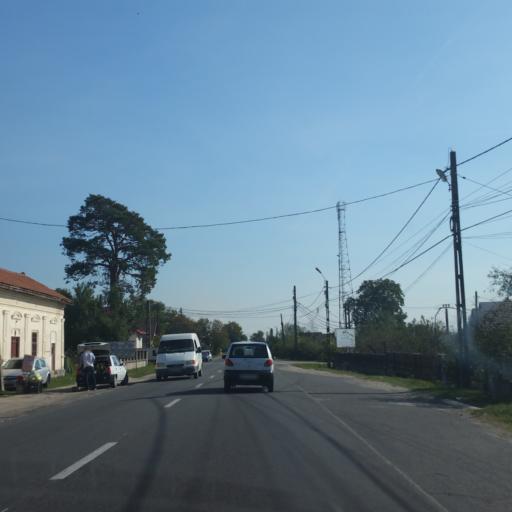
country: RO
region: Arges
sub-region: Comuna Baiculesti
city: Baiculesti
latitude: 45.0915
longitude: 24.6748
